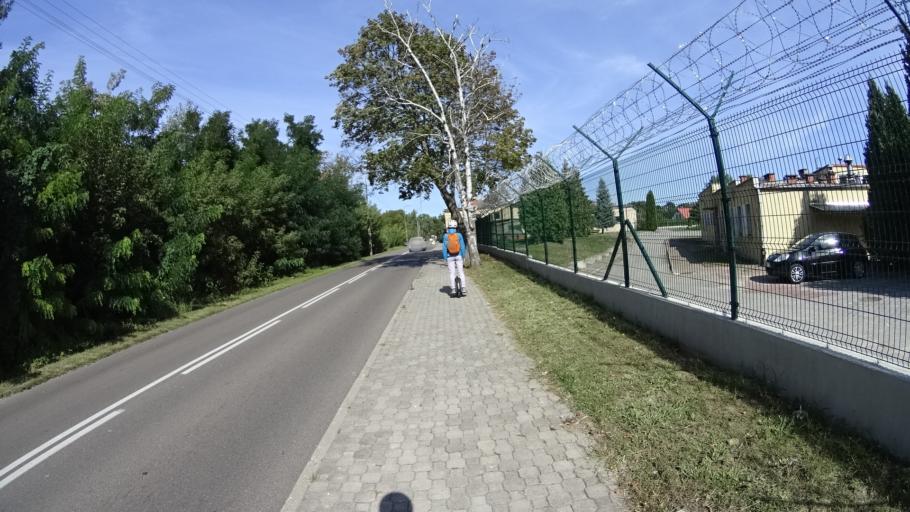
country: PL
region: Masovian Voivodeship
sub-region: Powiat legionowski
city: Bialobrzegi
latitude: 52.4443
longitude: 21.0563
